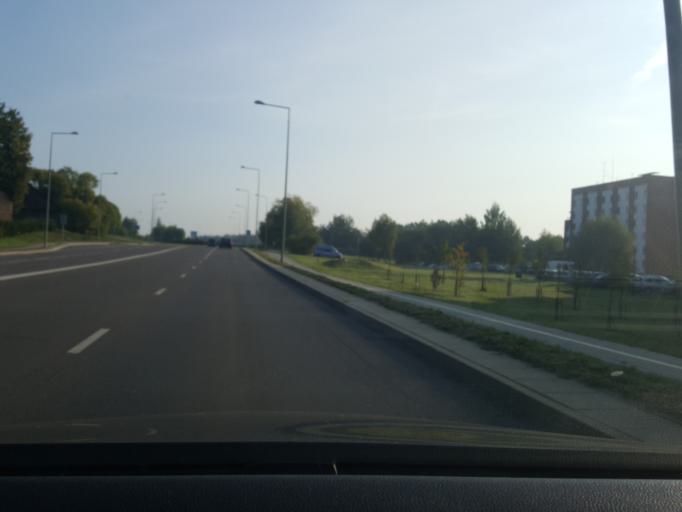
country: LT
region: Alytaus apskritis
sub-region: Alytus
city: Alytus
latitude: 54.4229
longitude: 24.0315
